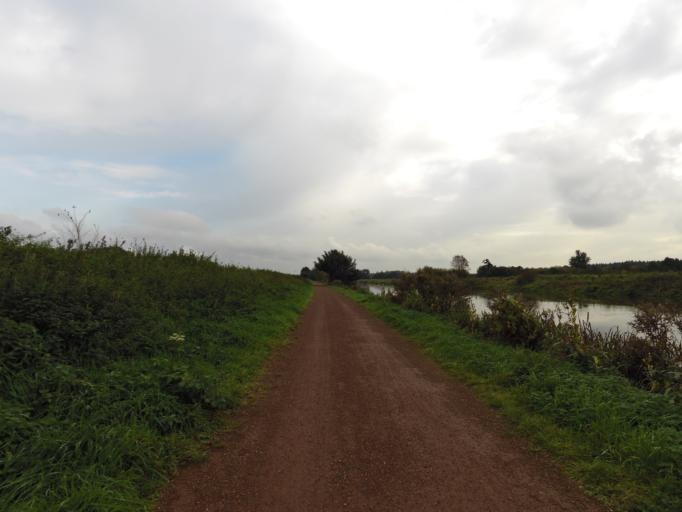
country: DE
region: North Rhine-Westphalia
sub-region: Regierungsbezirk Munster
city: Isselburg
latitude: 51.8518
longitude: 6.4805
